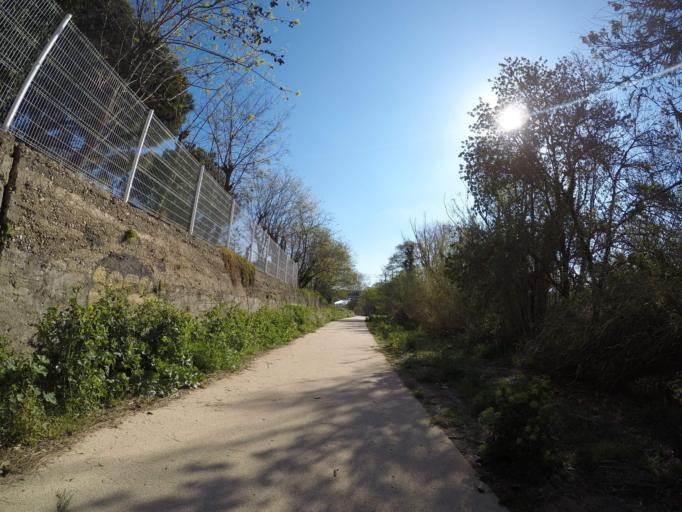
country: FR
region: Languedoc-Roussillon
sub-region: Departement des Pyrenees-Orientales
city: Perpignan
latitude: 42.7007
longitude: 2.8758
